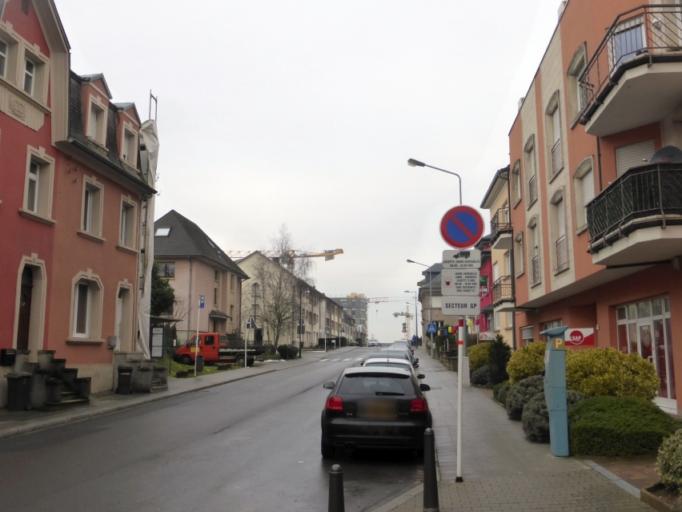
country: LU
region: Luxembourg
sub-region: Canton de Luxembourg
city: Luxembourg
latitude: 49.5927
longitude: 6.1213
